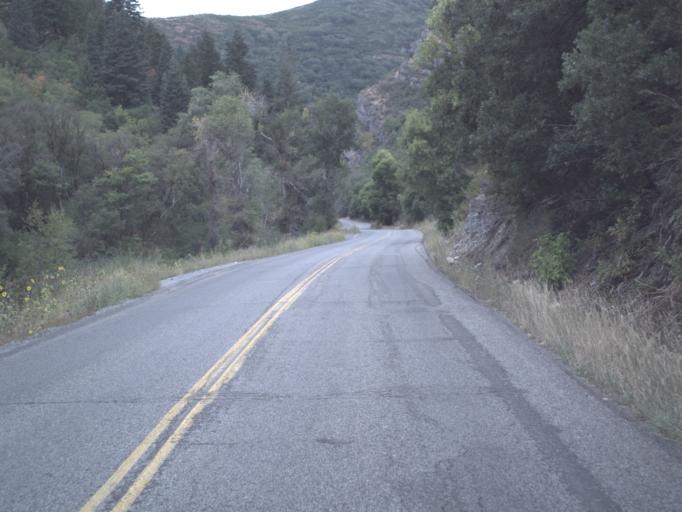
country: US
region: Utah
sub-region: Utah County
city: Orem
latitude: 40.3689
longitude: -111.5625
